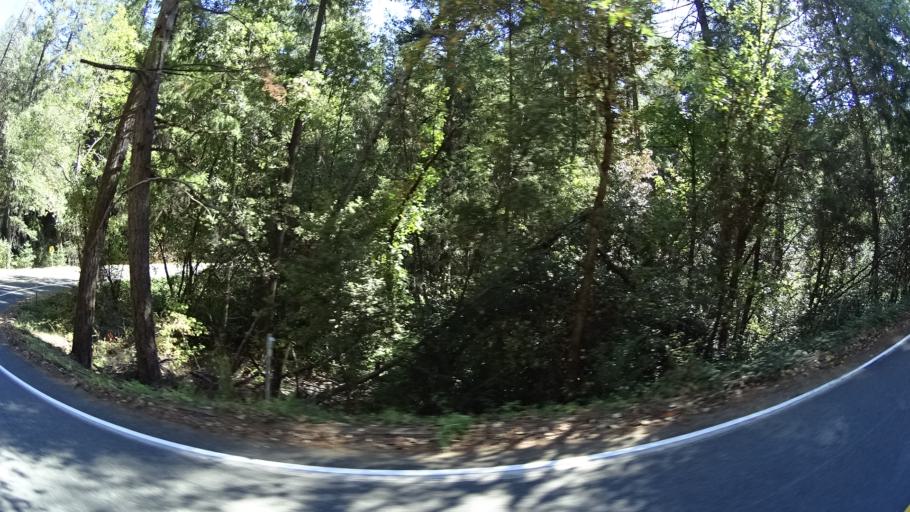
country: US
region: California
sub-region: Siskiyou County
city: Happy Camp
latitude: 41.3764
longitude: -123.4504
